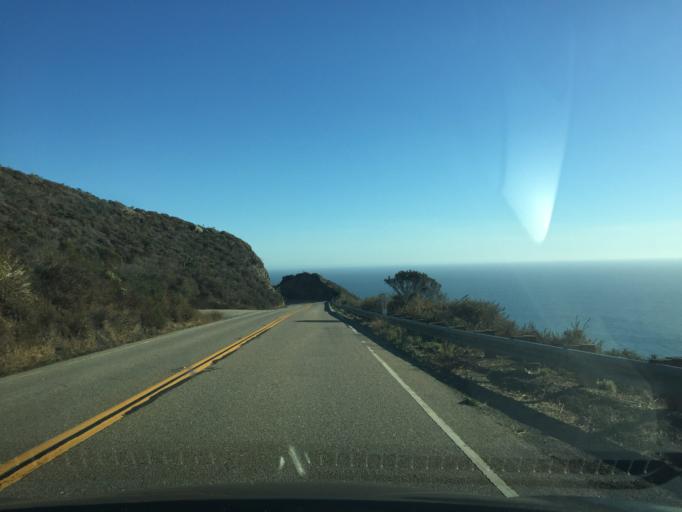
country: US
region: California
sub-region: San Luis Obispo County
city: Cambria
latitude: 35.8158
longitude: -121.3700
